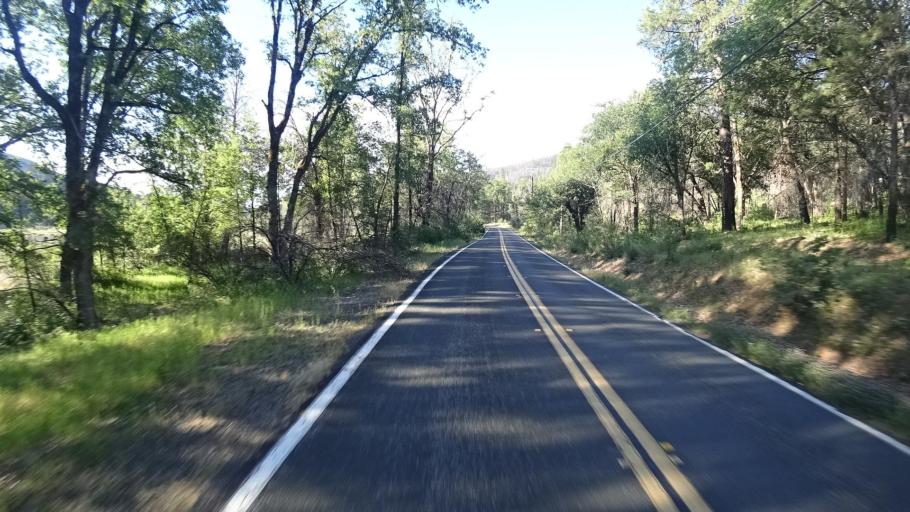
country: US
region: California
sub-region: Lake County
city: Upper Lake
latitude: 39.2289
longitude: -122.9439
